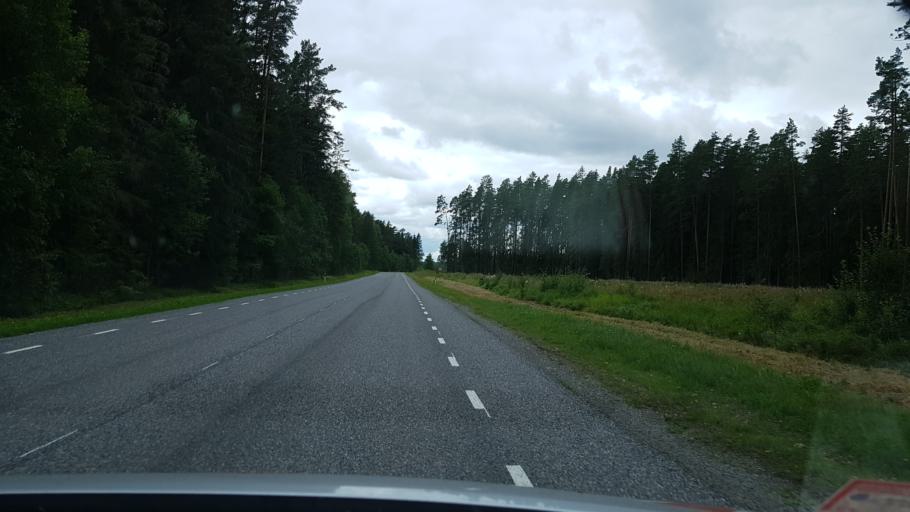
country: EE
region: Polvamaa
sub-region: Polva linn
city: Polva
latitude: 58.1724
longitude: 27.1312
